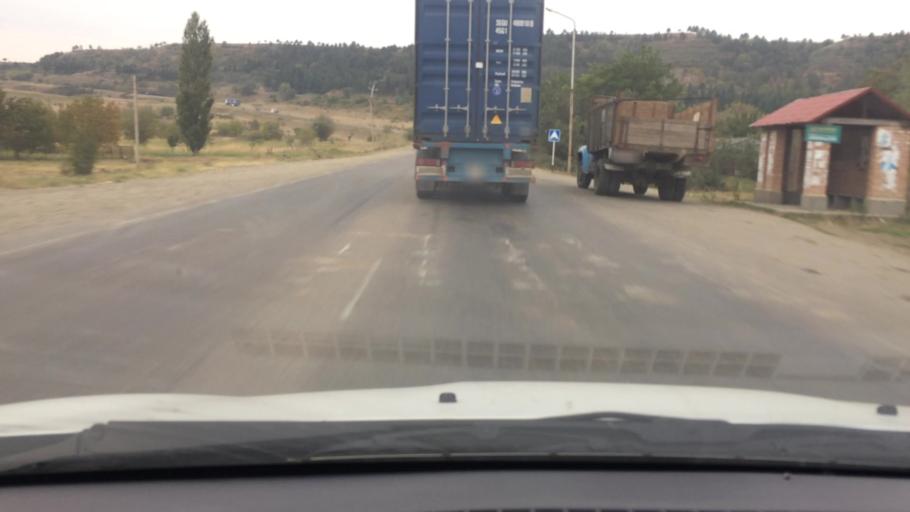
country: GE
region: T'bilisi
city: Tbilisi
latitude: 41.6045
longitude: 44.7810
